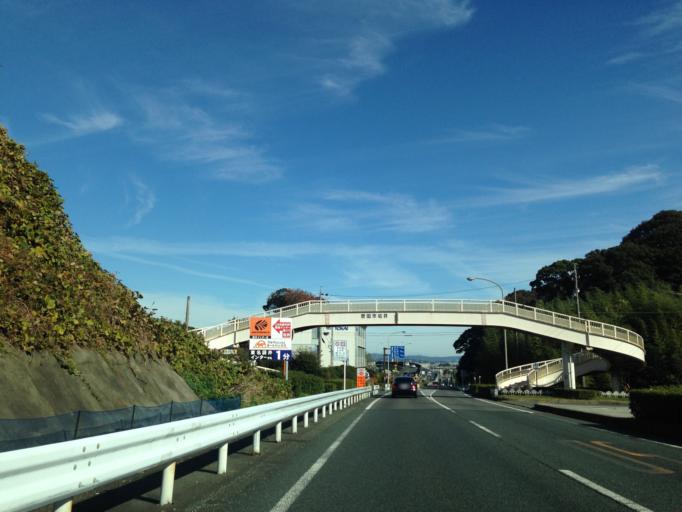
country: JP
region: Shizuoka
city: Fukuroi
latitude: 34.7358
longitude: 137.8807
